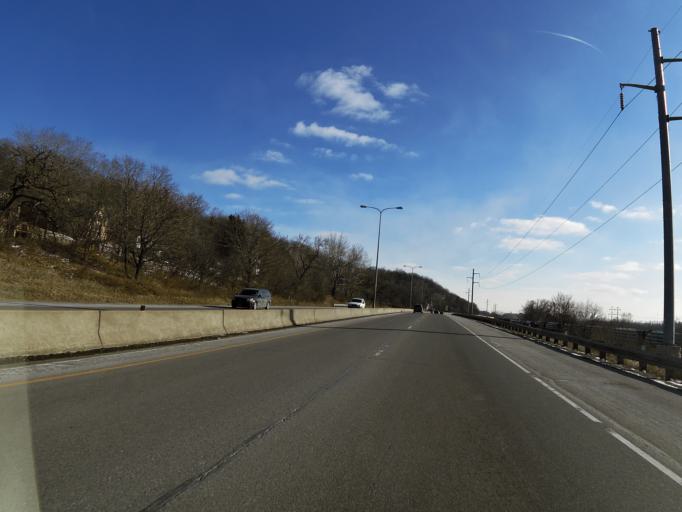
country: US
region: Minnesota
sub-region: Dakota County
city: South Saint Paul
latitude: 44.9203
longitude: -93.0167
